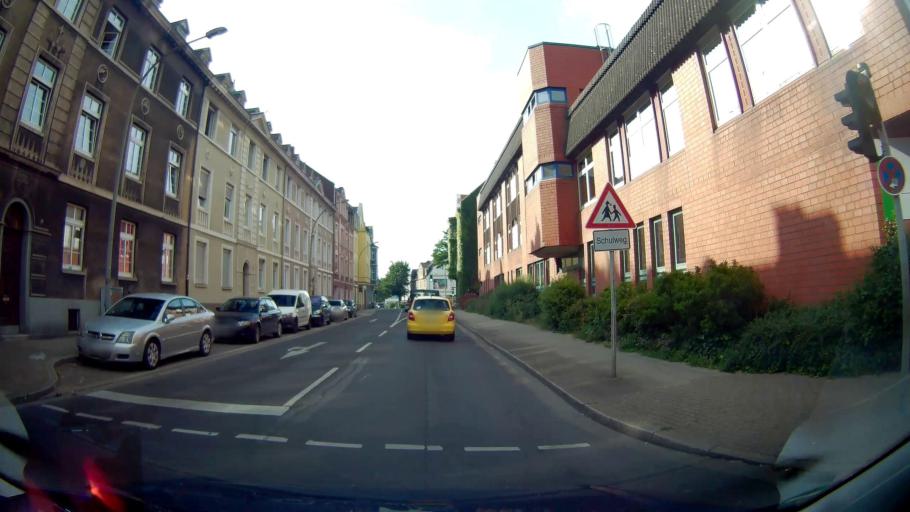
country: DE
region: North Rhine-Westphalia
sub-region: Regierungsbezirk Arnsberg
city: Herne
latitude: 51.5427
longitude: 7.2255
